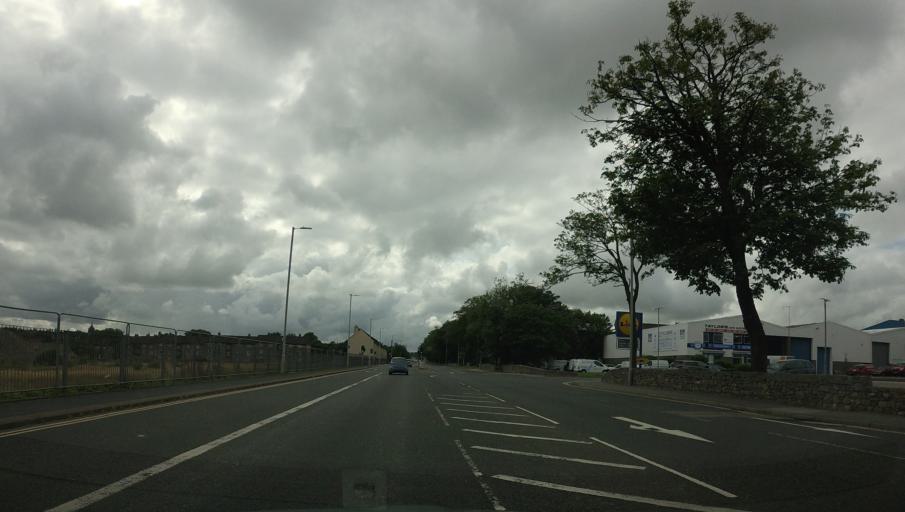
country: GB
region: Scotland
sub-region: Aberdeen City
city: Cults
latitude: 57.1512
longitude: -2.1620
